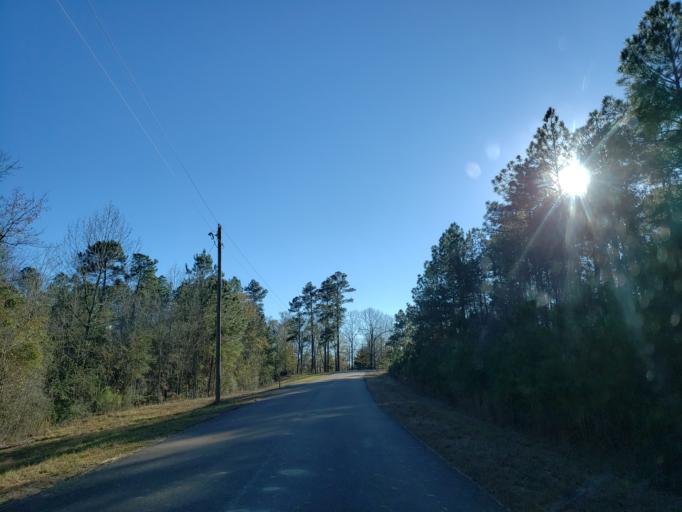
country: US
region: Mississippi
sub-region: Lamar County
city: Sumrall
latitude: 31.3552
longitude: -89.4759
